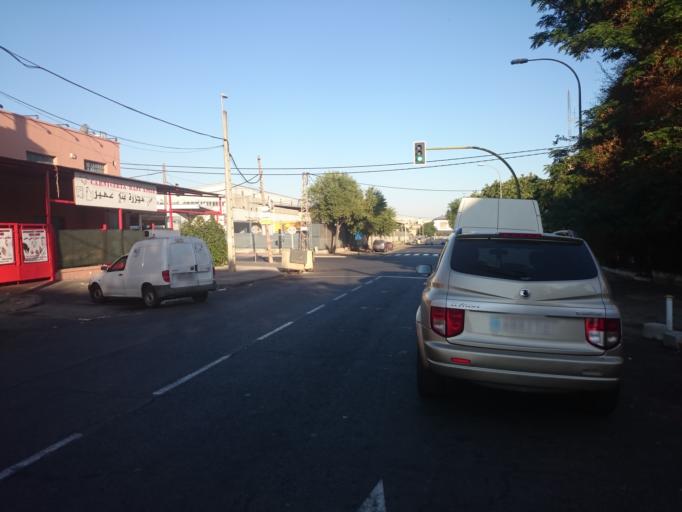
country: ES
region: Andalusia
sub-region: Provincia de Sevilla
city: Sevilla
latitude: 37.3885
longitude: -5.9536
